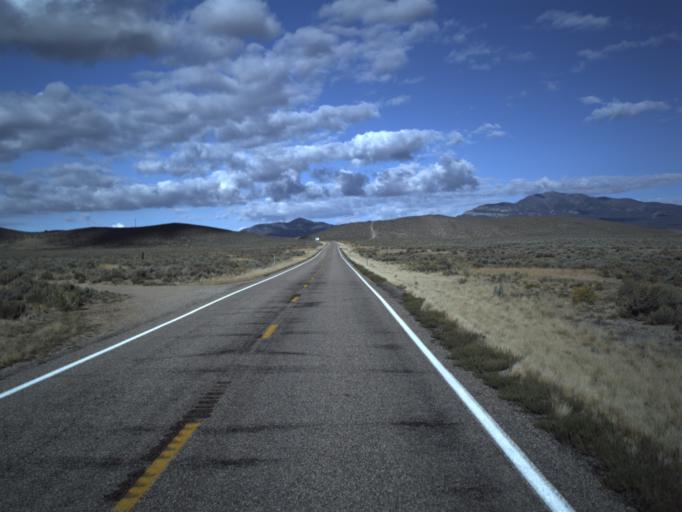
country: US
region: Utah
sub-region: Beaver County
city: Milford
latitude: 38.4204
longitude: -113.0980
